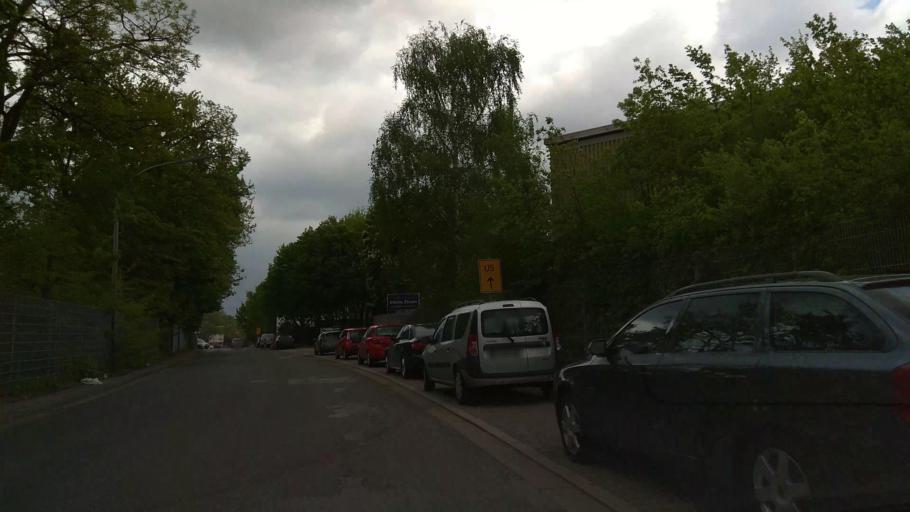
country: DE
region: North Rhine-Westphalia
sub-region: Regierungsbezirk Munster
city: Gelsenkirchen
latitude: 51.5494
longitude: 7.0915
